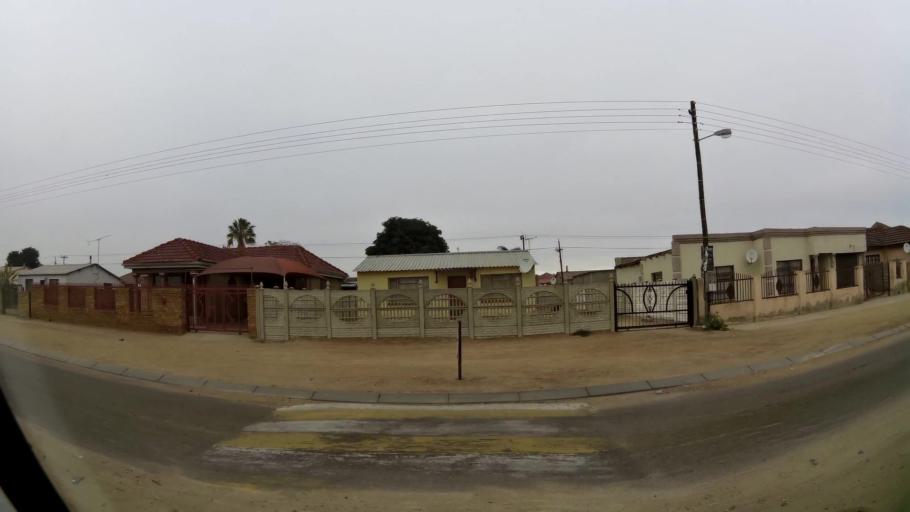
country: ZA
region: Limpopo
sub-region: Capricorn District Municipality
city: Polokwane
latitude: -23.8355
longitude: 29.3903
